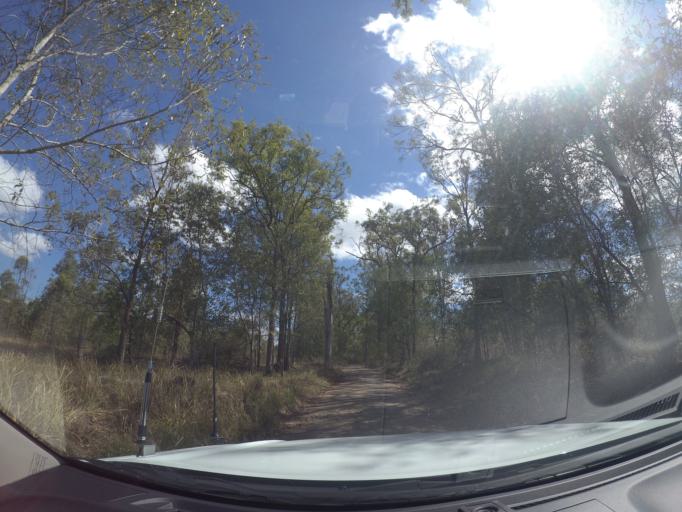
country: AU
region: Queensland
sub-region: Logan
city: Cedar Vale
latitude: -27.8409
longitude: 152.9744
